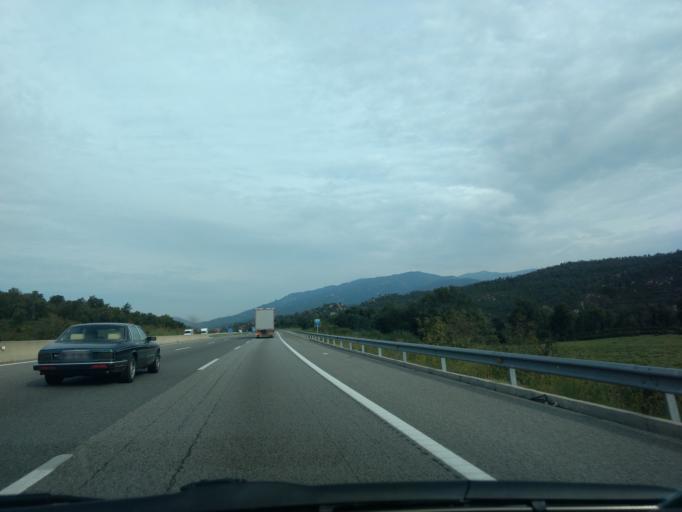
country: ES
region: Catalonia
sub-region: Provincia de Girona
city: Capmany
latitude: 42.3785
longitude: 2.8863
